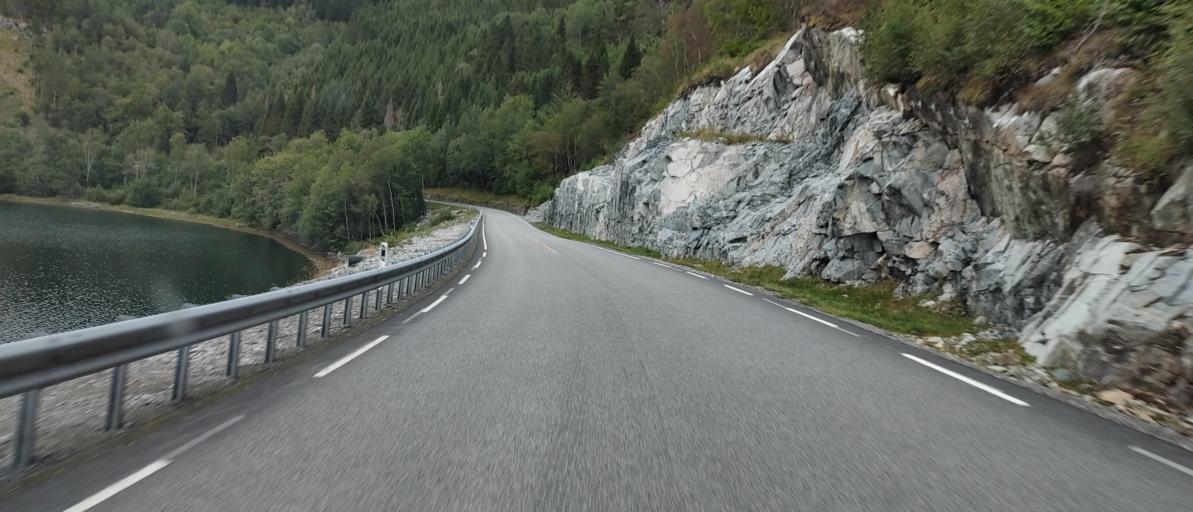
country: NO
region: More og Romsdal
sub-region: Rauma
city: Andalsnes
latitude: 62.5790
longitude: 7.5417
